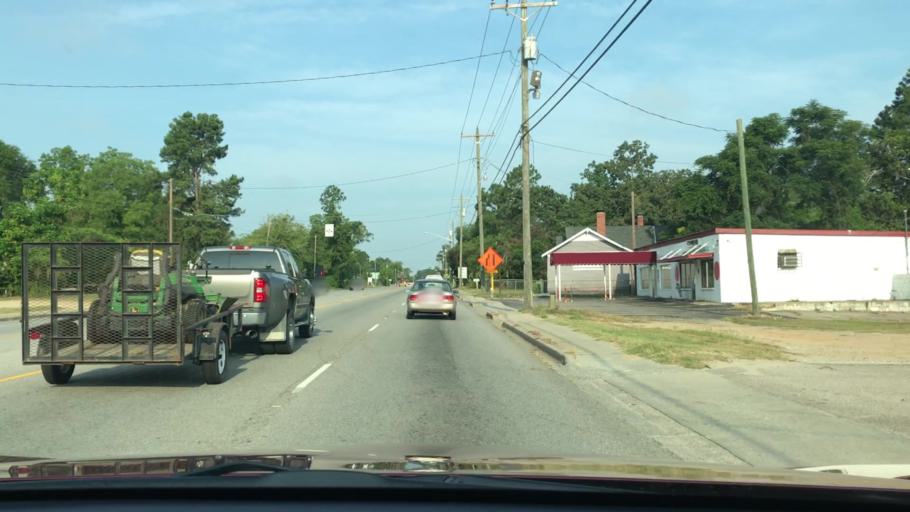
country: US
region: South Carolina
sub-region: Orangeburg County
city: Edisto
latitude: 33.4809
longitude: -80.8949
